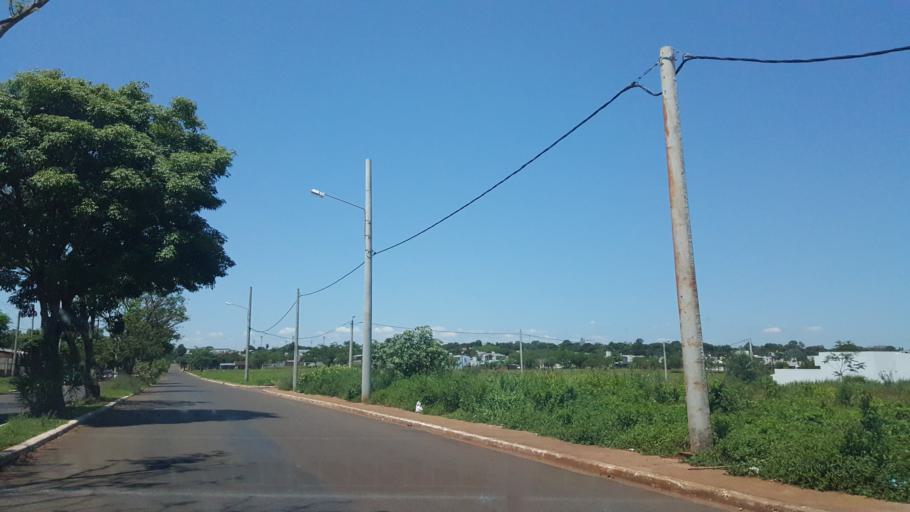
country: AR
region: Misiones
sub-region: Departamento de Capital
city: Posadas
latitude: -27.3814
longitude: -55.9260
